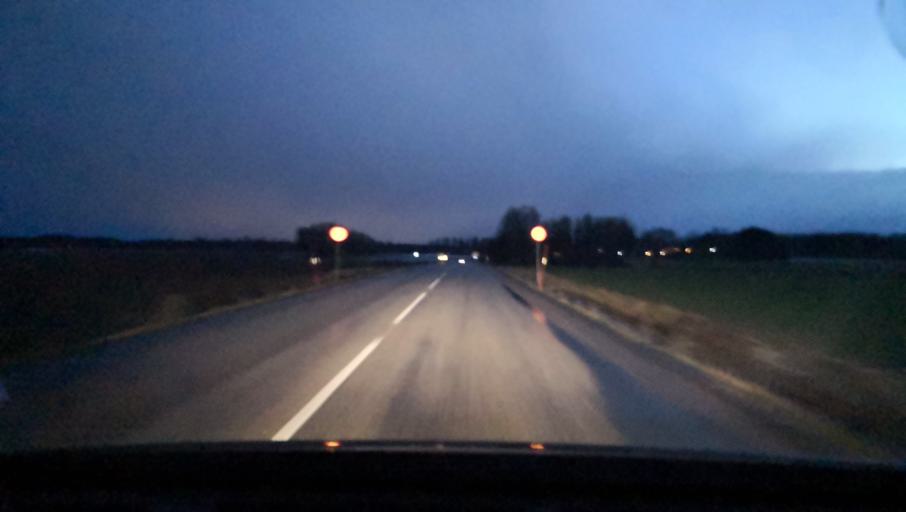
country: SE
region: Vaestmanland
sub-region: Vasteras
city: Skultuna
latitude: 59.7699
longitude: 16.4612
